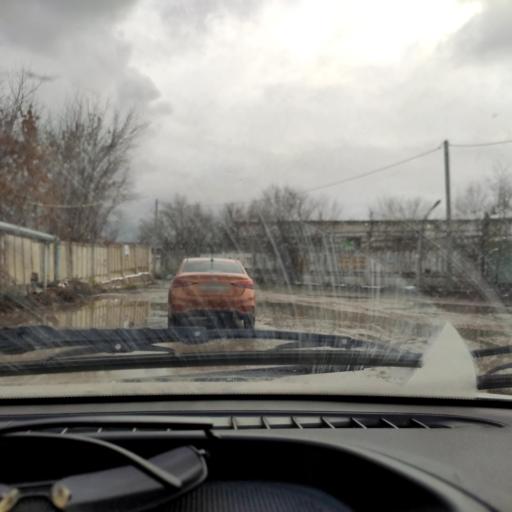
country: RU
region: Samara
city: Zhigulevsk
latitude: 53.4852
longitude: 49.4915
